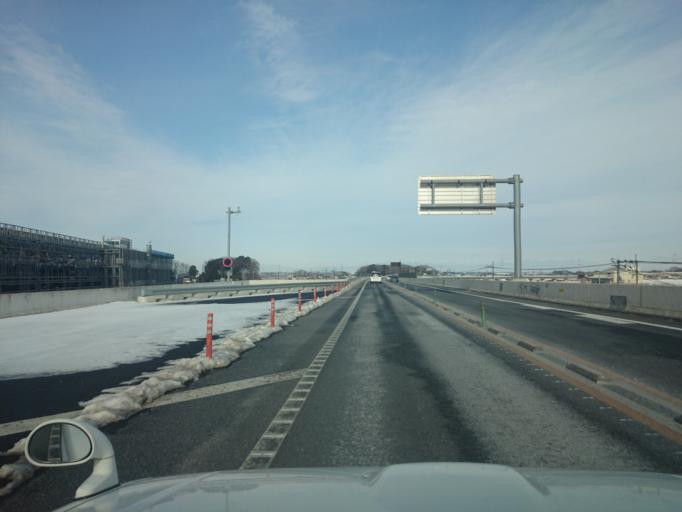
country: JP
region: Ibaraki
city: Sakai
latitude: 36.0993
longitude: 139.7594
